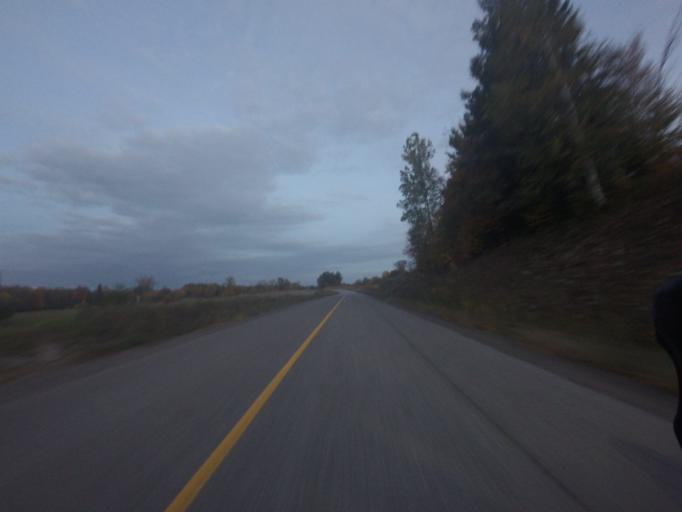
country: CA
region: Ontario
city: Renfrew
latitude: 45.3395
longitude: -76.9140
